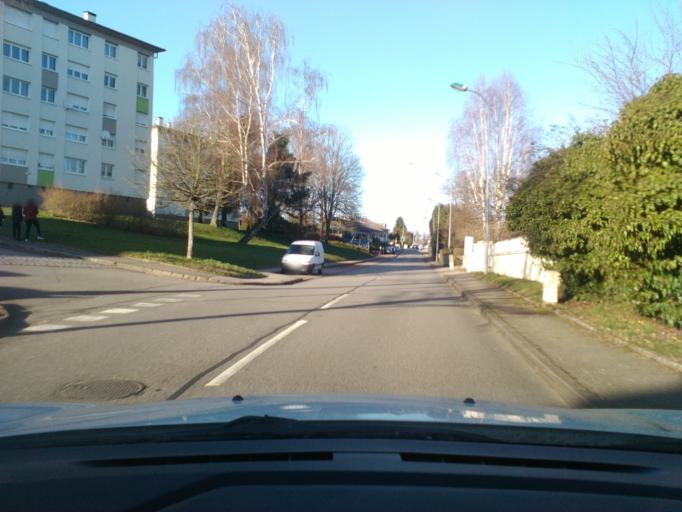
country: FR
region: Lorraine
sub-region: Departement des Vosges
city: Epinal
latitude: 48.1841
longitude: 6.4638
